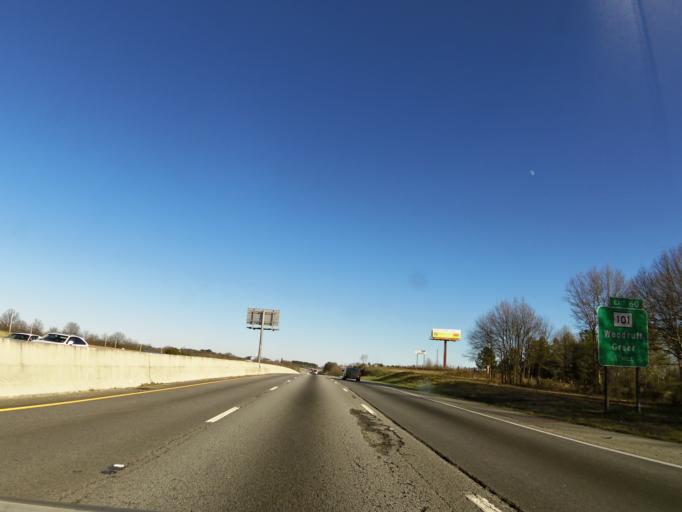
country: US
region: South Carolina
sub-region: Spartanburg County
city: Duncan
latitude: 34.8882
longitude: -82.1777
